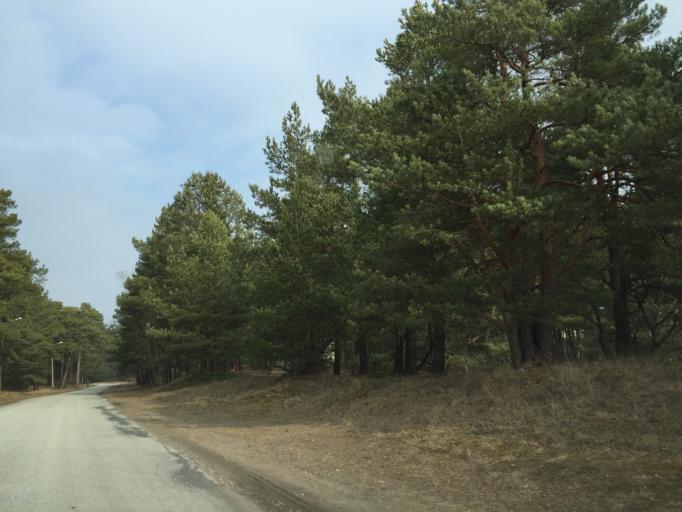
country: LV
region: Salacgrivas
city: Ainazi
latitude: 57.9220
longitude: 24.3887
